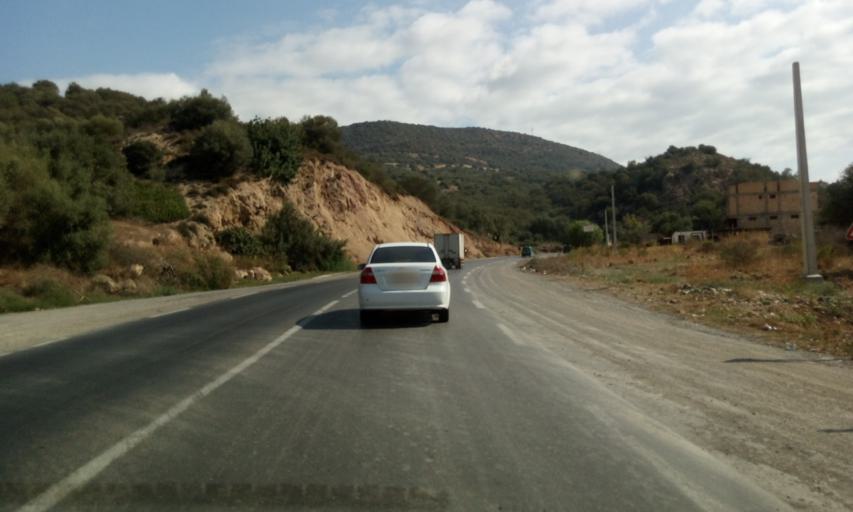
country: DZ
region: Bejaia
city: el hed
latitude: 36.6535
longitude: 4.7986
